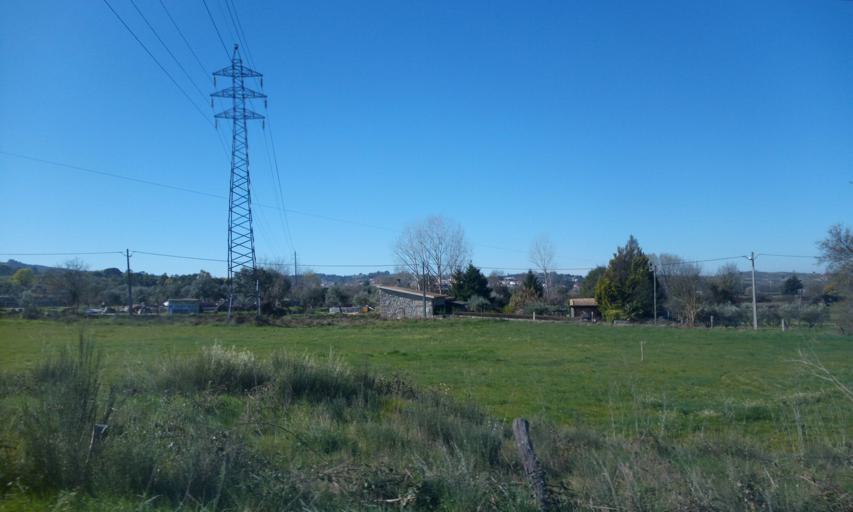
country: PT
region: Guarda
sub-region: Fornos de Algodres
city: Fornos de Algodres
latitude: 40.5305
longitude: -7.5596
